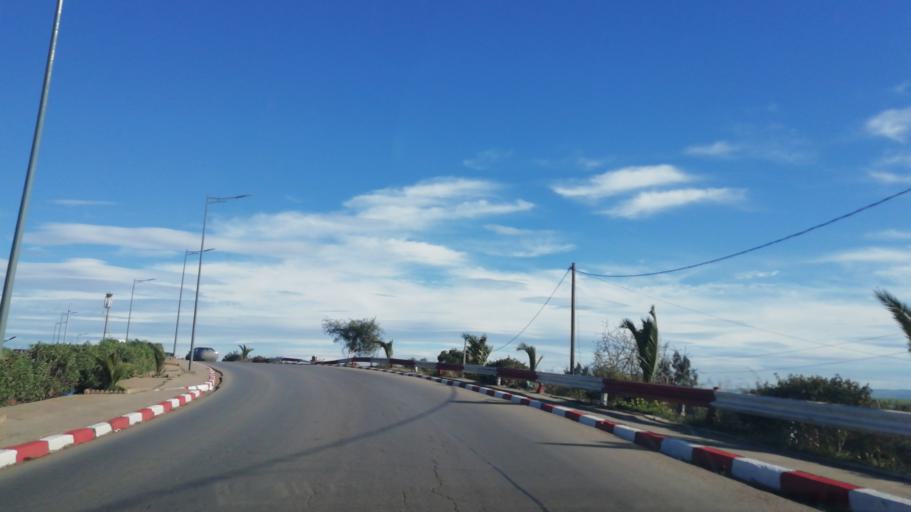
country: DZ
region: Oran
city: Es Senia
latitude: 35.6112
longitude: -0.5814
